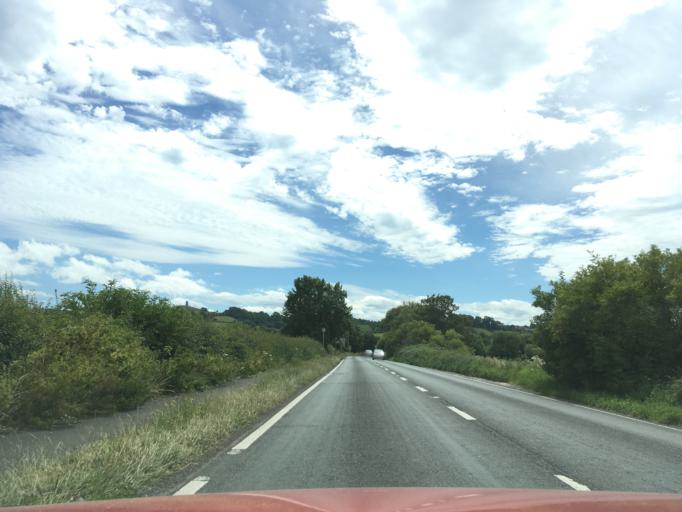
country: GB
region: England
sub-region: Somerset
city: Glastonbury
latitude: 51.1648
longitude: -2.6991
